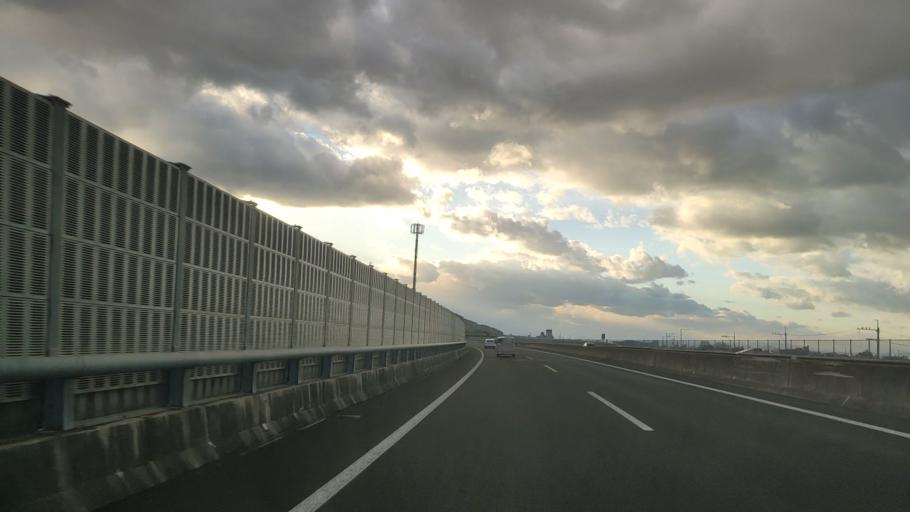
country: JP
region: Ehime
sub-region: Shikoku-chuo Shi
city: Matsuyama
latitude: 33.7887
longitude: 132.8234
